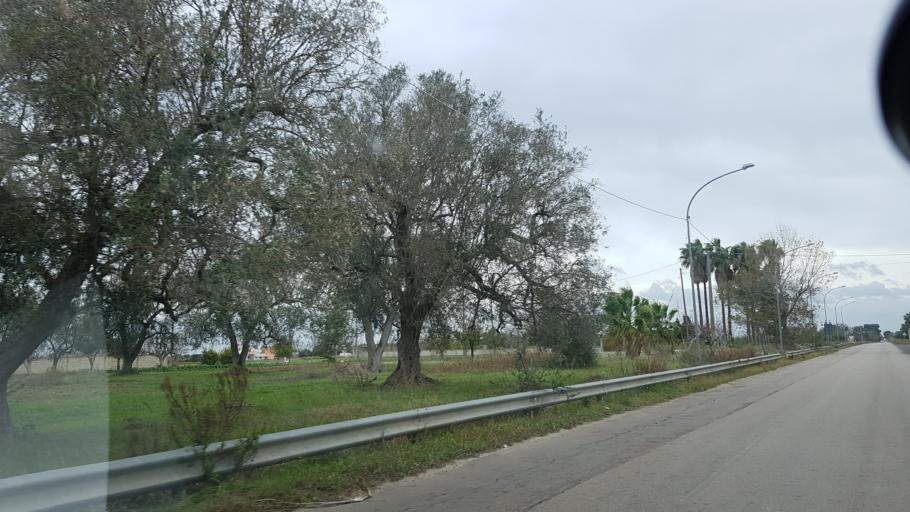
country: IT
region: Apulia
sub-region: Provincia di Brindisi
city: San Pancrazio Salentino
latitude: 40.4160
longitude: 17.8480
